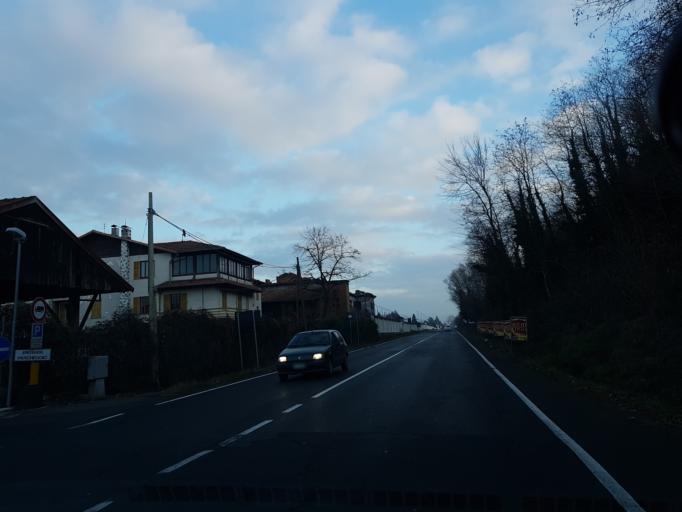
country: IT
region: Piedmont
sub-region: Provincia di Alessandria
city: Novi Ligure
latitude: 44.7555
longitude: 8.7988
